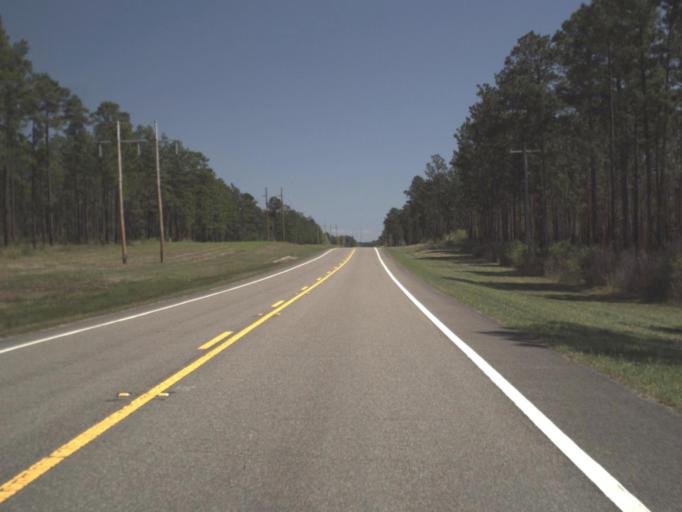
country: US
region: Florida
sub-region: Santa Rosa County
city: Point Baker
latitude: 30.8690
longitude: -86.9243
